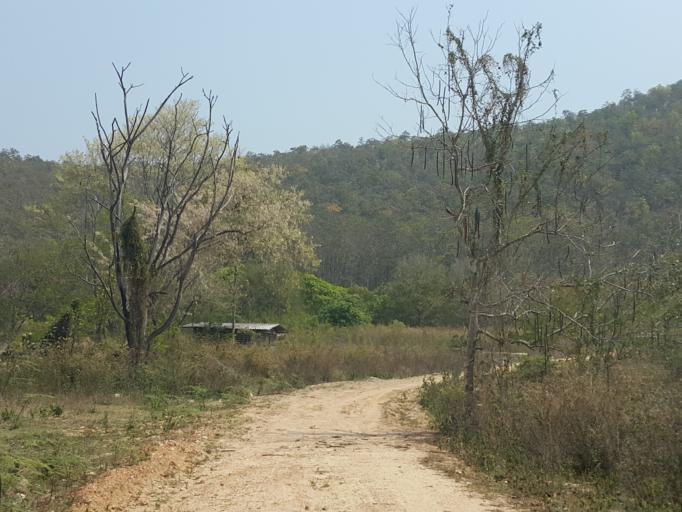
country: TH
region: Chiang Mai
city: Mae On
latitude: 18.7065
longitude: 99.2040
